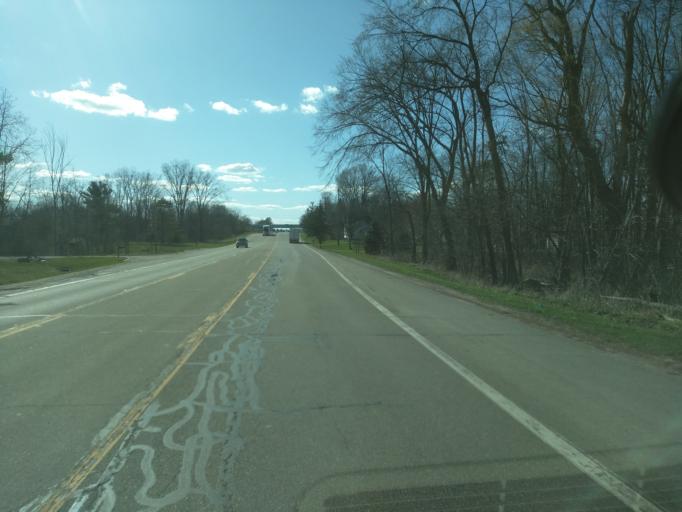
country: US
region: Michigan
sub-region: Eaton County
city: Waverly
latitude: 42.7828
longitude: -84.6583
